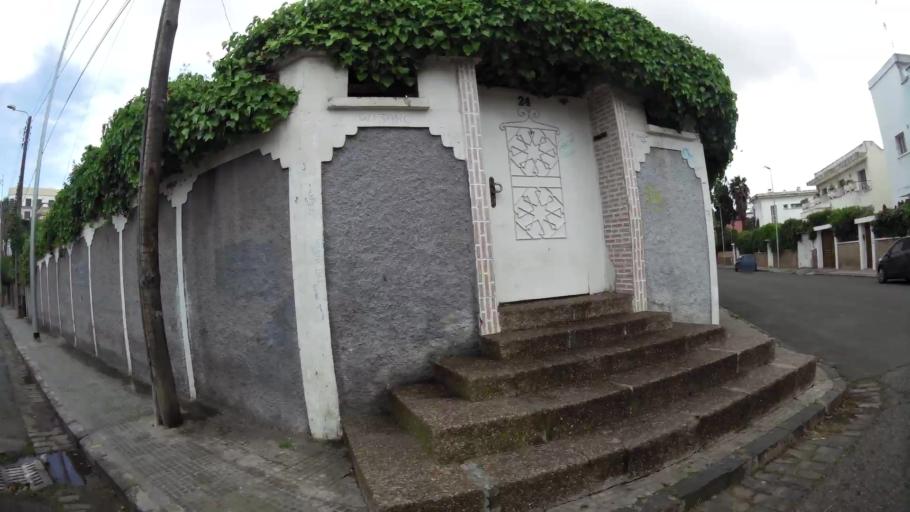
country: MA
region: Grand Casablanca
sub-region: Casablanca
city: Casablanca
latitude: 33.5713
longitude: -7.6214
